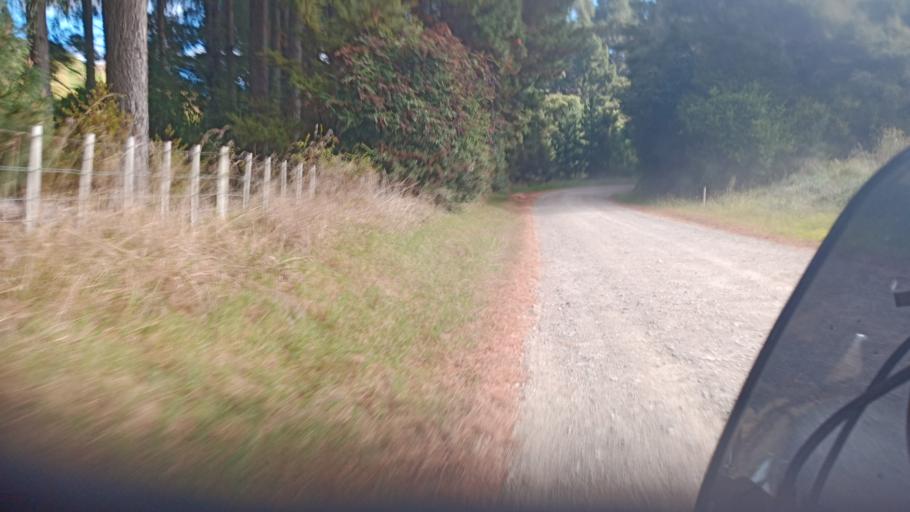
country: NZ
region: Gisborne
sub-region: Gisborne District
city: Gisborne
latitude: -38.4220
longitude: 177.7073
